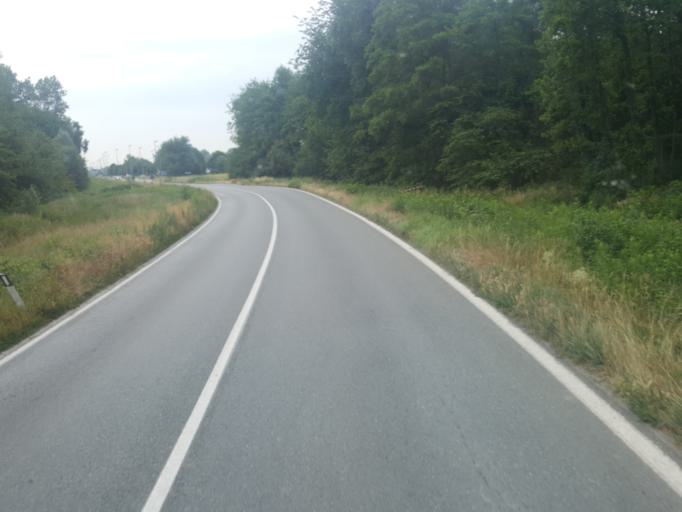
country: IT
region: Piedmont
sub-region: Provincia di Torino
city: Candiolo
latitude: 44.9711
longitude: 7.5636
